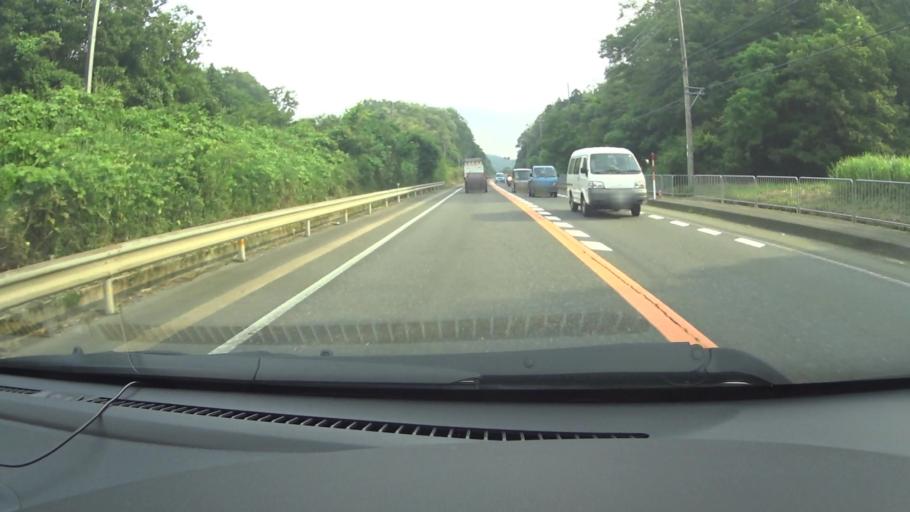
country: JP
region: Kyoto
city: Maizuru
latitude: 35.3674
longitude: 135.3191
